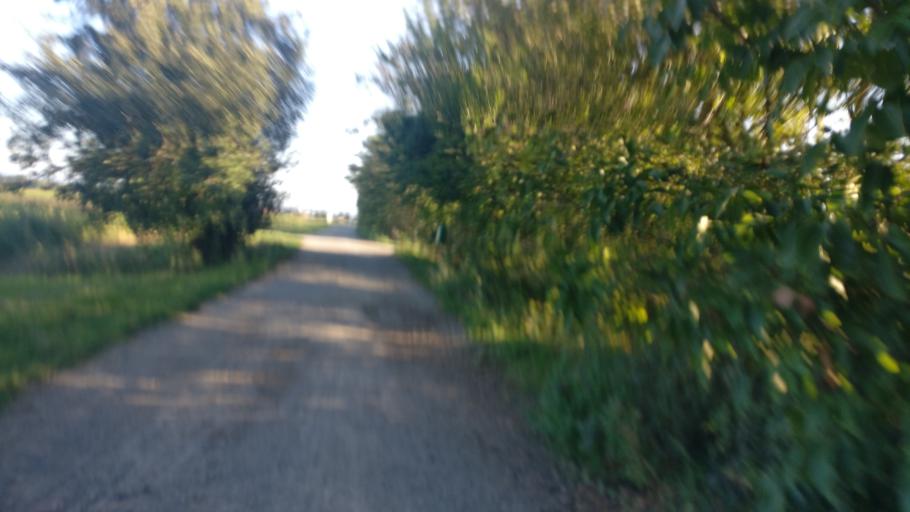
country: AT
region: Lower Austria
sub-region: Politischer Bezirk Wien-Umgebung
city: Lanzendorf
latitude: 48.1166
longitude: 16.4346
